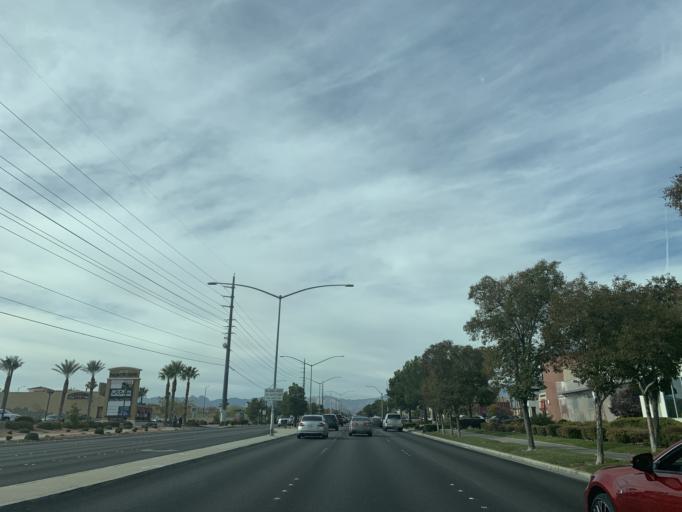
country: US
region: Nevada
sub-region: Clark County
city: Summerlin South
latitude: 36.1591
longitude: -115.2851
